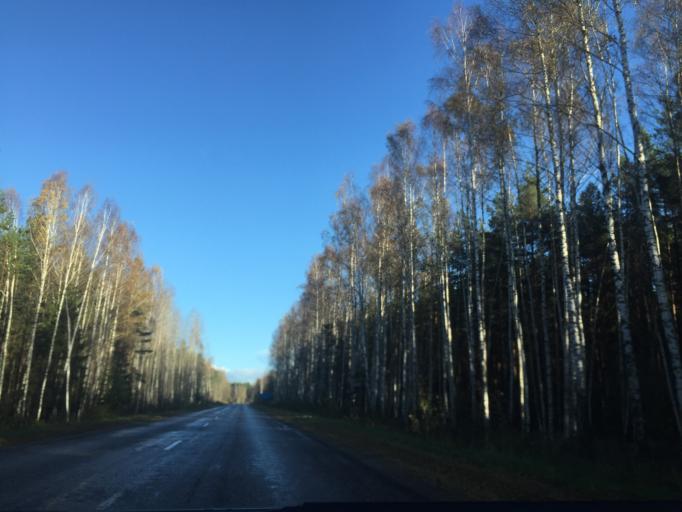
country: LV
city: Tireli
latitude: 56.9213
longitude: 23.5251
